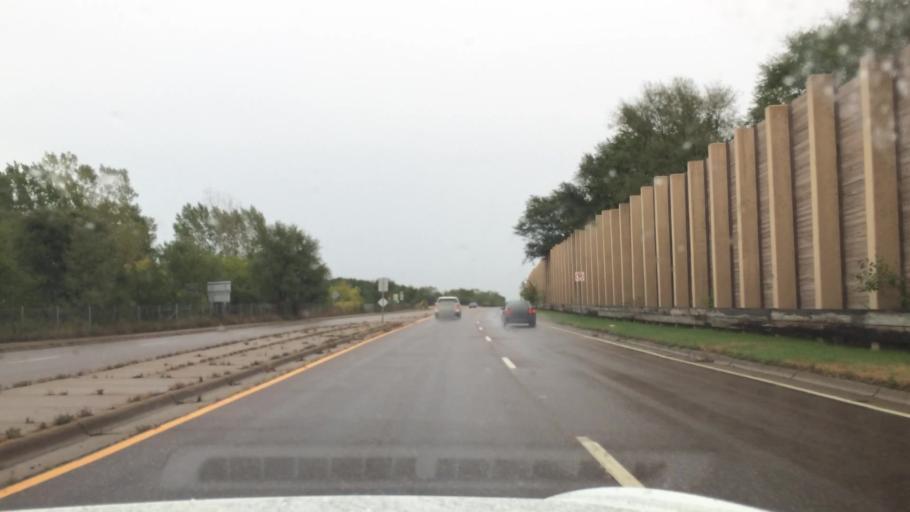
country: US
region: Minnesota
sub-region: Ramsey County
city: Mounds View
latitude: 45.1249
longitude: -93.2168
